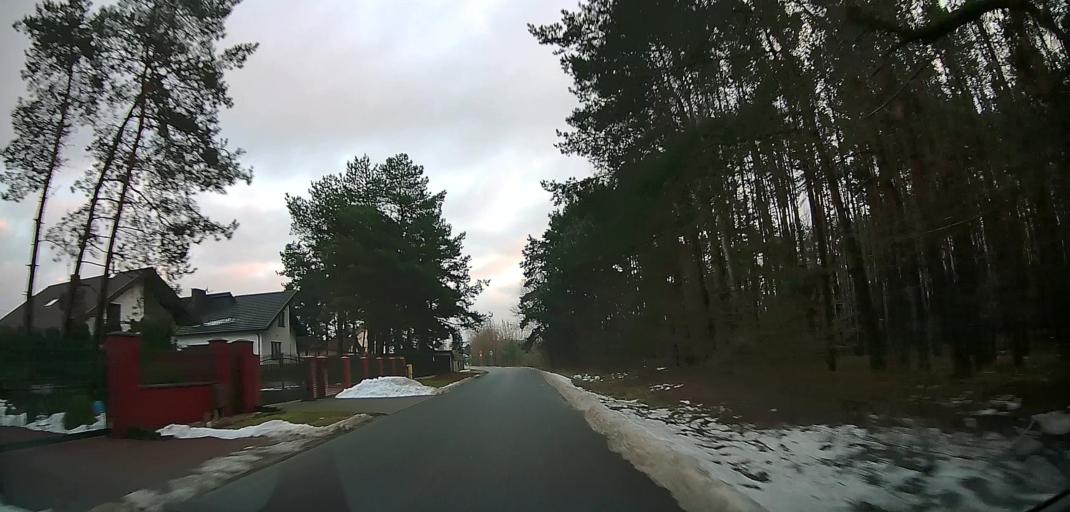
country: PL
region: Masovian Voivodeship
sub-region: Radom
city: Radom
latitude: 51.4514
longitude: 21.1316
